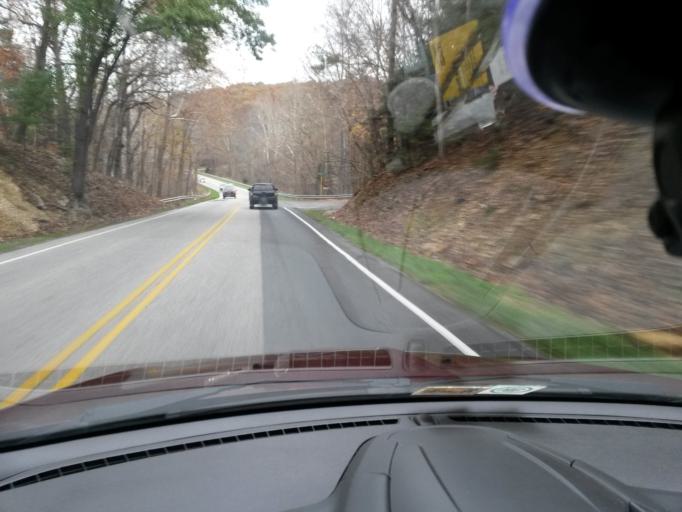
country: US
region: Virginia
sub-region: City of Buena Vista
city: Buena Vista
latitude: 37.6899
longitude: -79.3948
